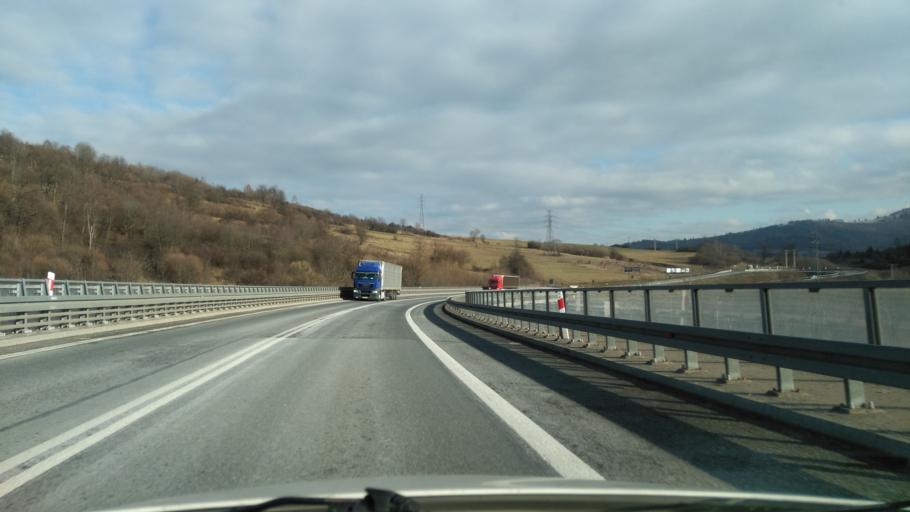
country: PL
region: Silesian Voivodeship
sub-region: Powiat zywiecki
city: Milowka
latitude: 49.5675
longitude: 19.0727
